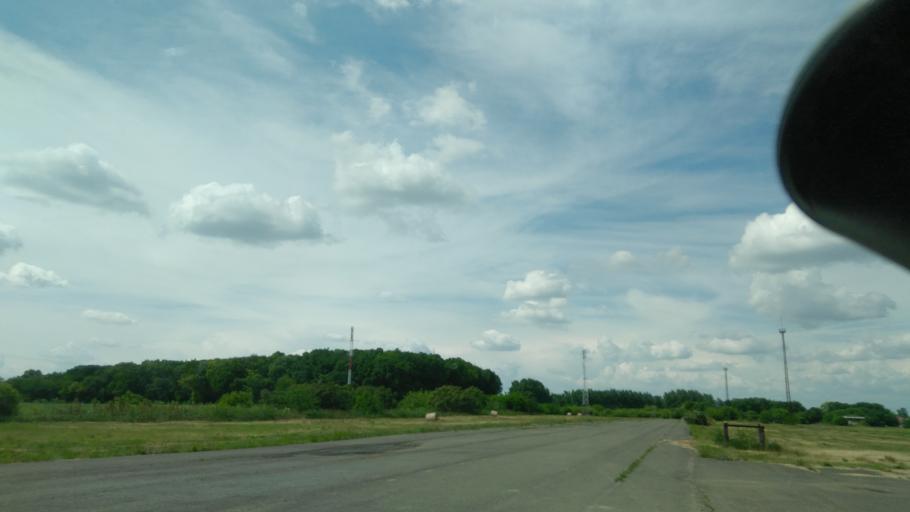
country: HU
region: Bekes
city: Mezohegyes
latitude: 46.3121
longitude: 20.8062
